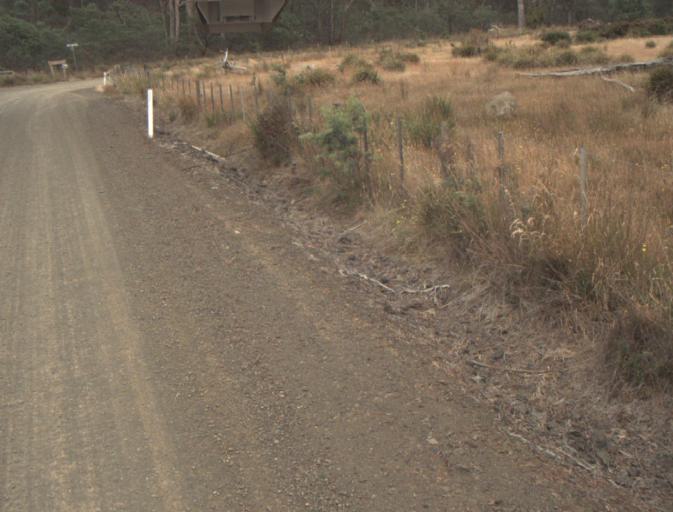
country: AU
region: Tasmania
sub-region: Northern Midlands
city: Evandale
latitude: -41.5201
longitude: 147.3804
